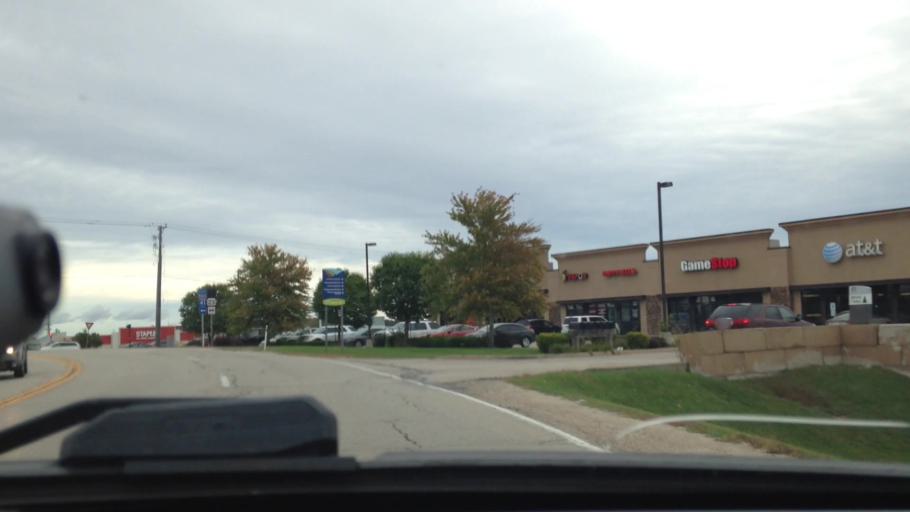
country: US
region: Wisconsin
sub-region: Fond du Lac County
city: North Fond du Lac
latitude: 43.7833
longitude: -88.4799
